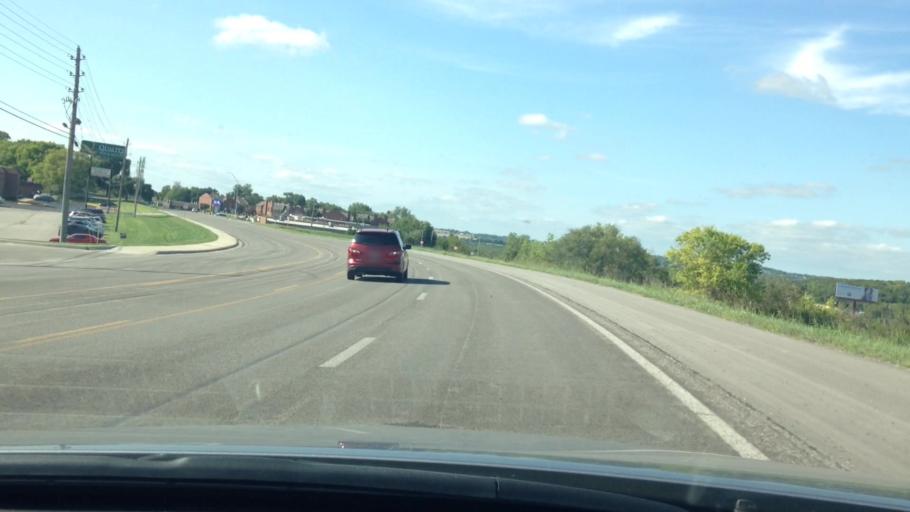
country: US
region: Missouri
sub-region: Platte County
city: Platte City
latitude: 39.3624
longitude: -94.7704
